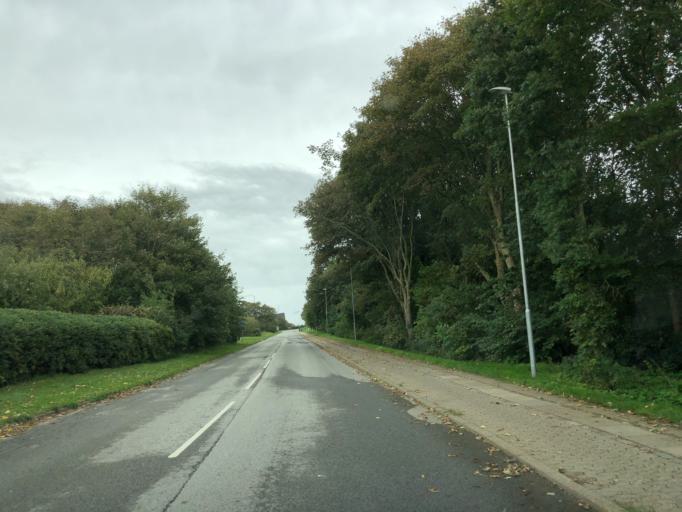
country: DK
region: North Denmark
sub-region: Thisted Kommune
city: Thisted
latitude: 56.9693
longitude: 8.6948
